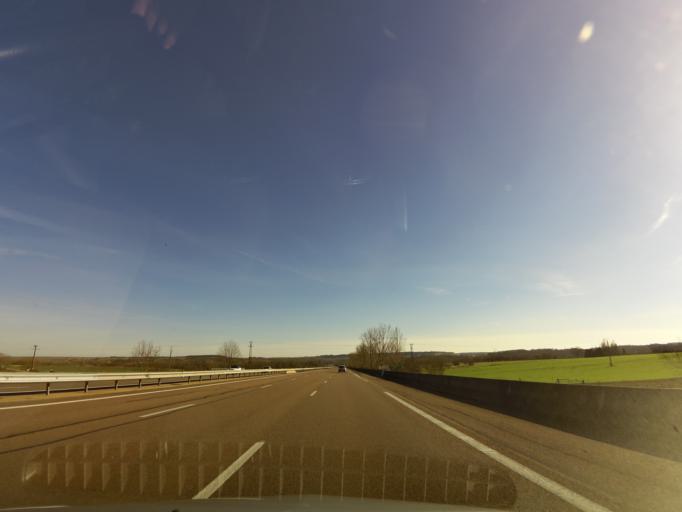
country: FR
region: Bourgogne
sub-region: Departement de l'Yonne
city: Fleury-la-Vallee
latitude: 47.8898
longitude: 3.4132
